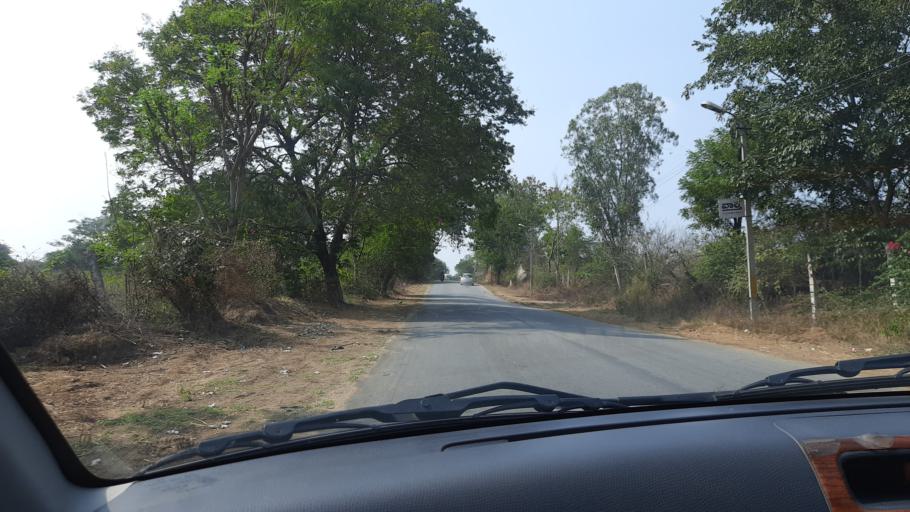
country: IN
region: Telangana
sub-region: Rangareddi
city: Lal Bahadur Nagar
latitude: 17.2753
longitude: 78.6627
